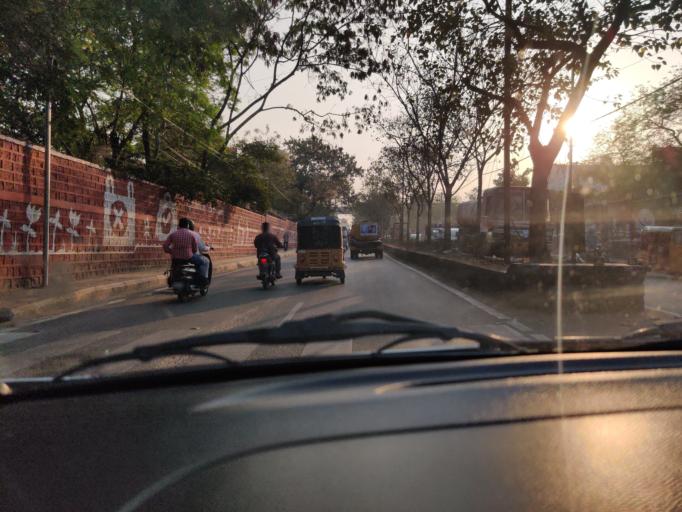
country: IN
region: Telangana
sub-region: Rangareddi
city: Uppal Kalan
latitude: 17.4208
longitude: 78.5435
